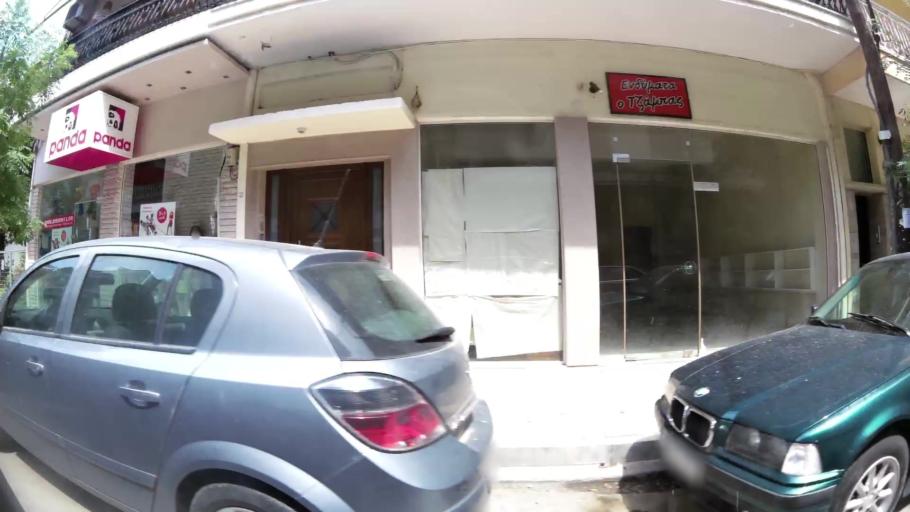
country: GR
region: Central Macedonia
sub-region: Nomos Pierias
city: Katerini
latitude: 40.2747
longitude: 22.5086
